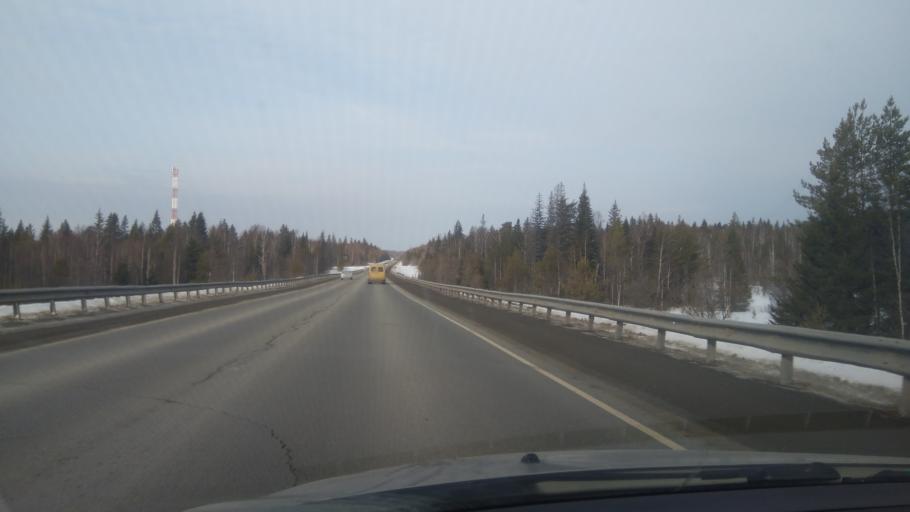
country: RU
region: Sverdlovsk
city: Nizhniye Sergi
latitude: 56.8238
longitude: 59.2999
